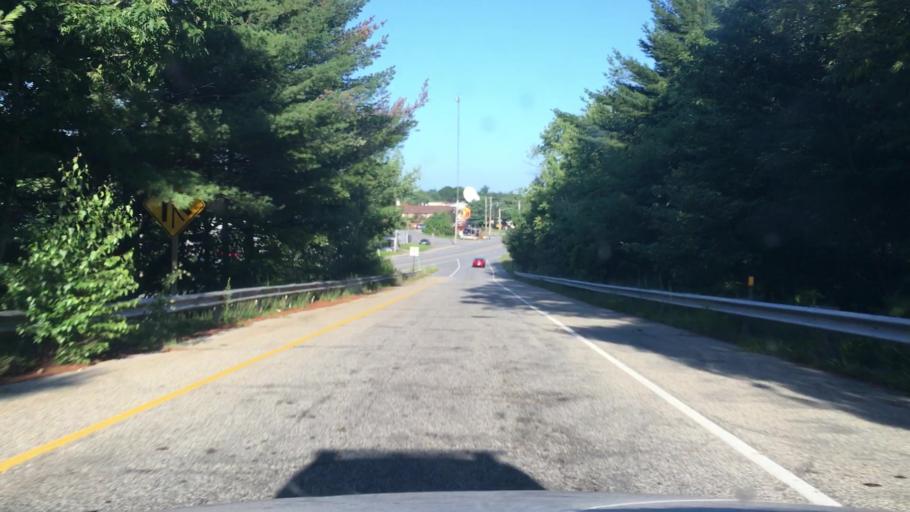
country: US
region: Maine
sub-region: Androscoggin County
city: Lewiston
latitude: 44.0748
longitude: -70.1816
